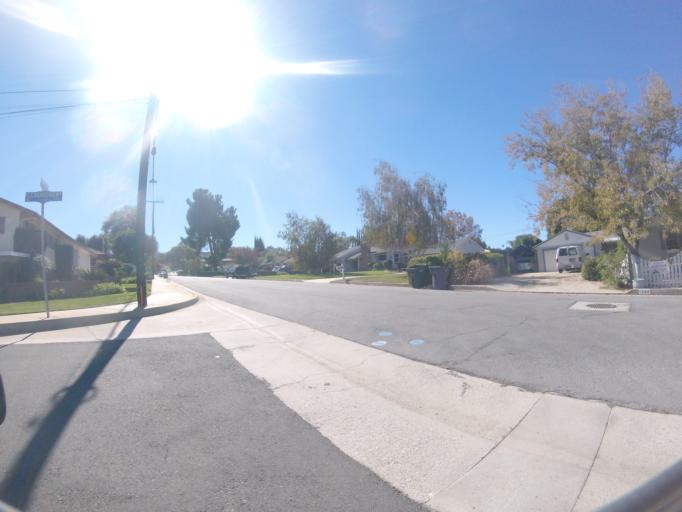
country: US
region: California
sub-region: San Bernardino County
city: Redlands
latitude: 34.0477
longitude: -117.1541
